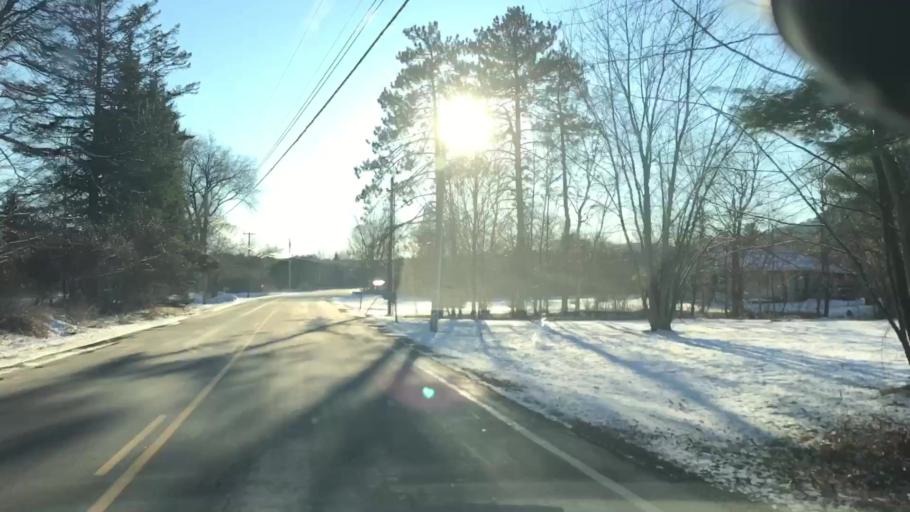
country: US
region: New Hampshire
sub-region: Grafton County
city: Orford
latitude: 43.9493
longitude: -72.1030
